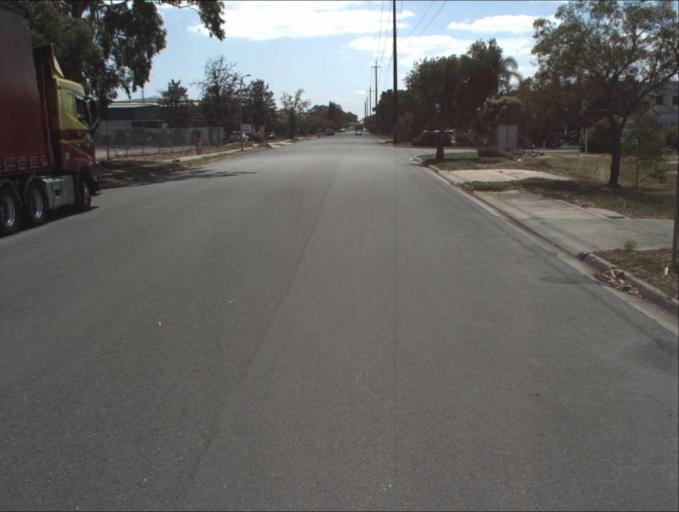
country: AU
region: South Australia
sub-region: Port Adelaide Enfield
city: Blair Athol
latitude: -34.8552
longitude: 138.5700
